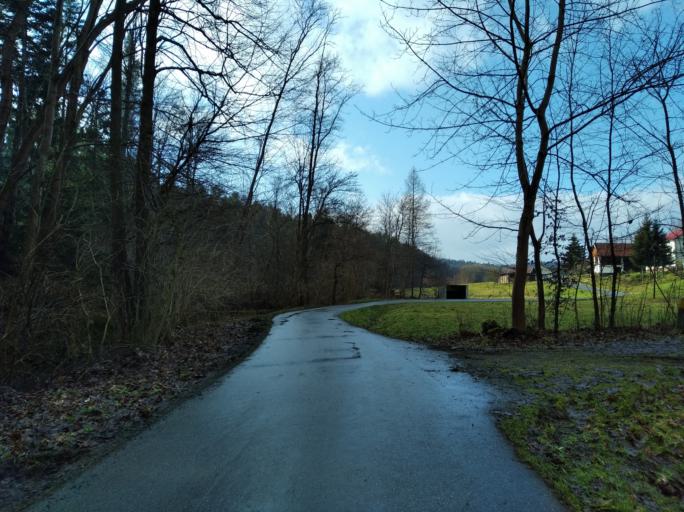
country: PL
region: Subcarpathian Voivodeship
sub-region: Powiat strzyzowski
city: Jawornik
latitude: 49.8325
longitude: 21.8806
